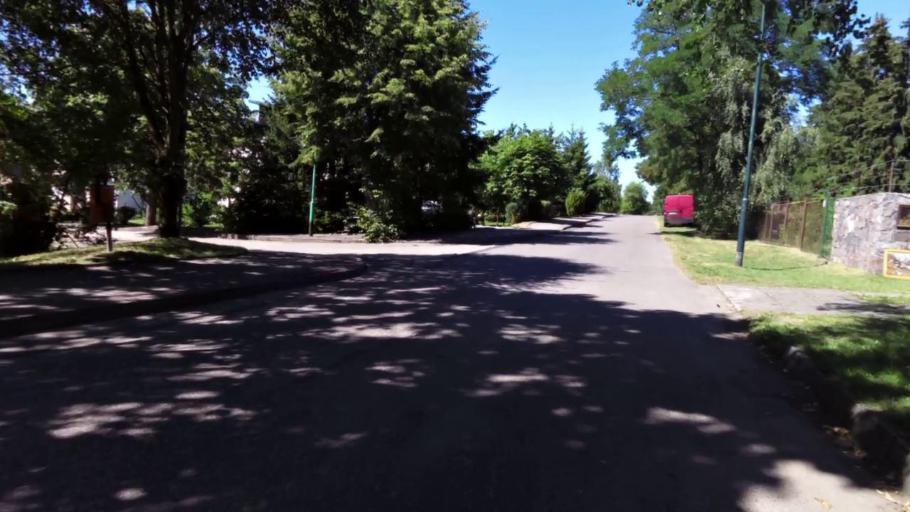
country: PL
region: West Pomeranian Voivodeship
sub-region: Powiat szczecinecki
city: Bialy Bor
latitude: 53.9024
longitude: 16.8305
